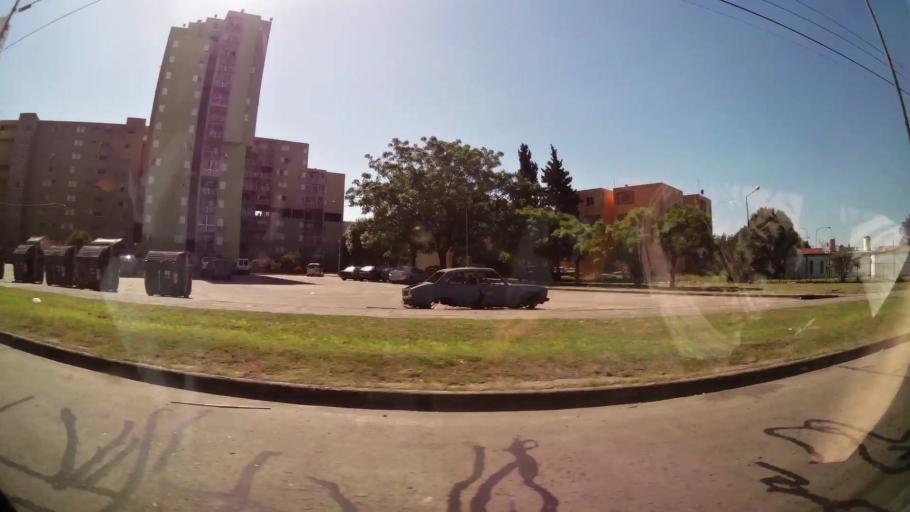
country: AR
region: Buenos Aires F.D.
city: Villa Lugano
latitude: -34.6674
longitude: -58.4417
